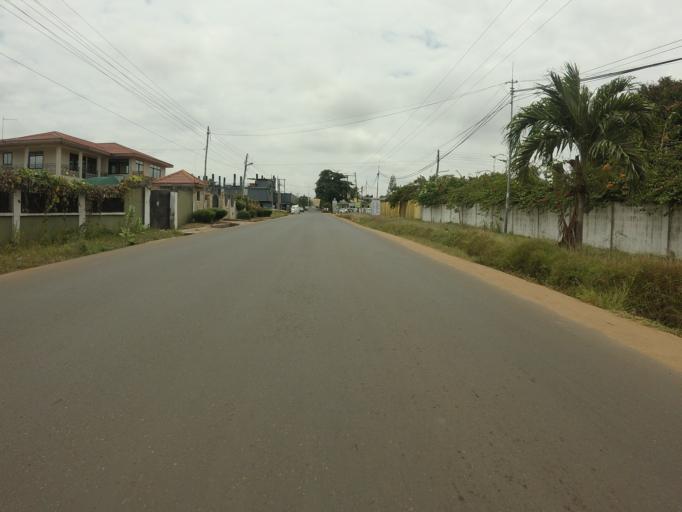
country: GH
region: Greater Accra
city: Nungua
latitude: 5.6059
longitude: -0.0935
